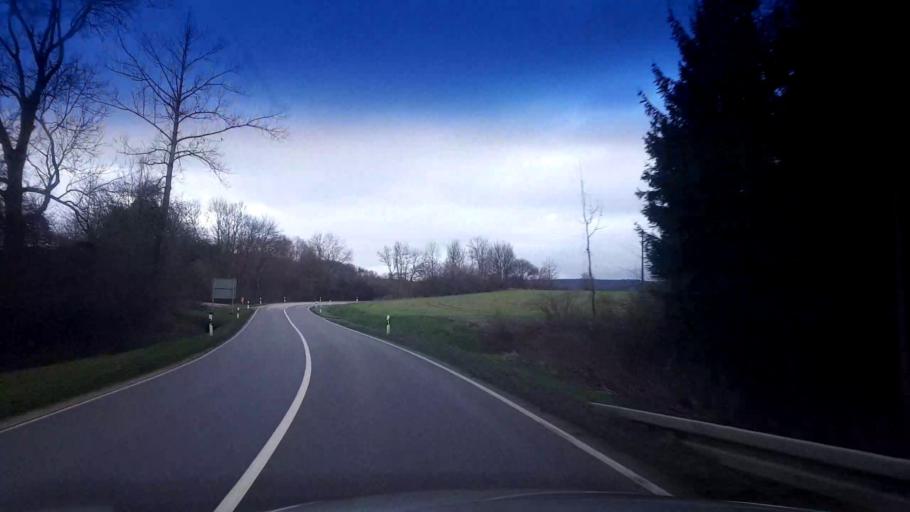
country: DE
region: Bavaria
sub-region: Upper Franconia
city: Buttenheim
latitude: 49.8081
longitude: 11.0660
